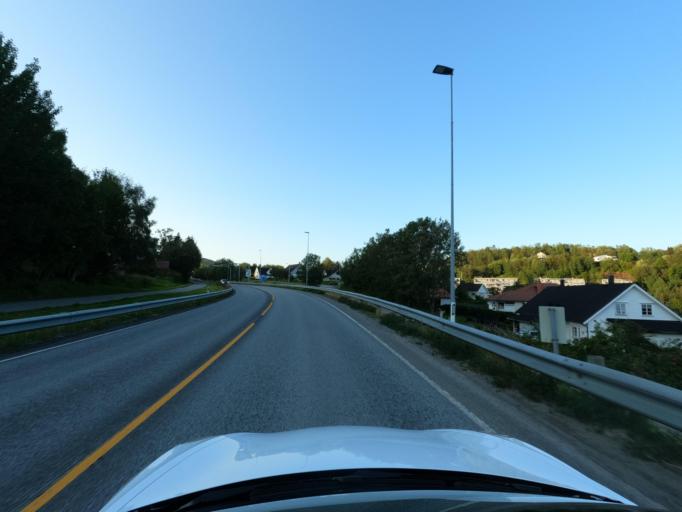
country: NO
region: Troms
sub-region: Harstad
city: Harstad
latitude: 68.7753
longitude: 16.5627
